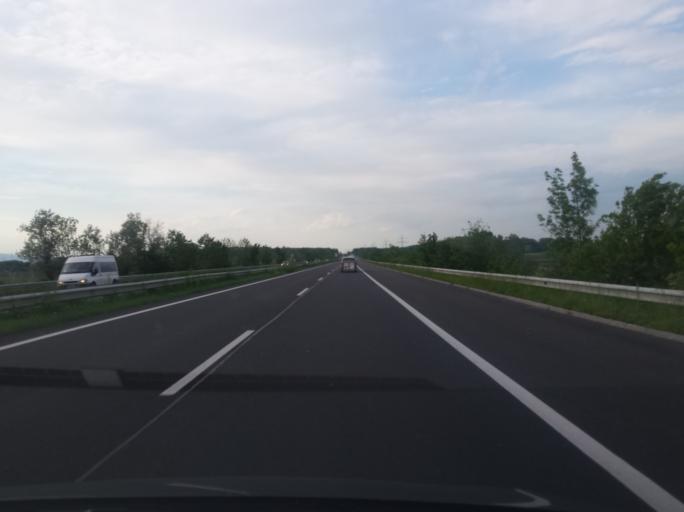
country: AT
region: Burgenland
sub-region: Eisenstadt-Umgebung
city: Hornstein
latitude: 47.8825
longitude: 16.4155
